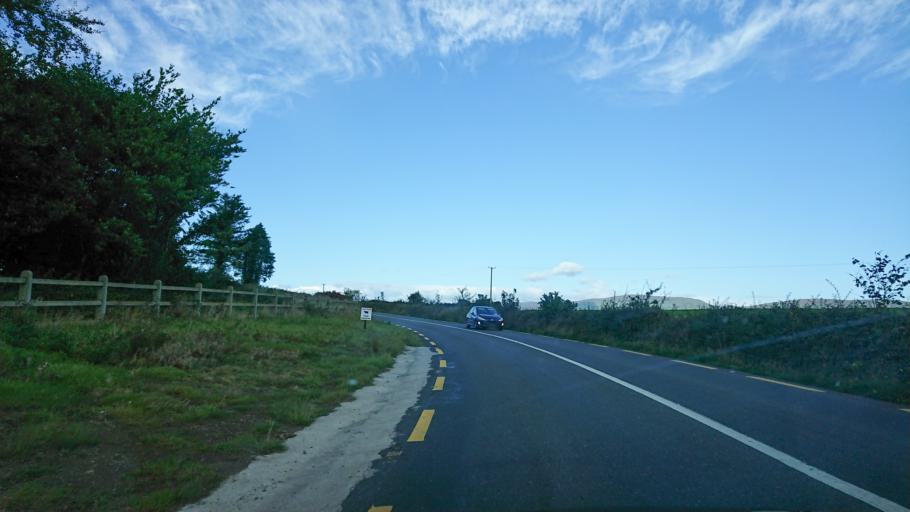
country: IE
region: Munster
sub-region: Waterford
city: Dungarvan
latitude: 52.1382
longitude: -7.6933
